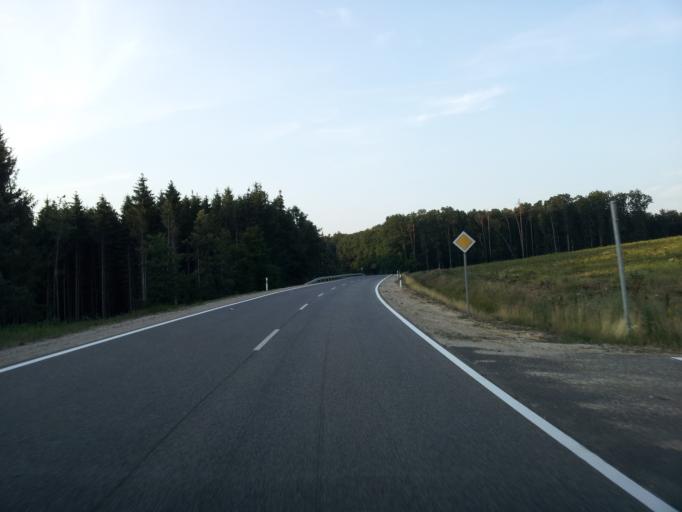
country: HU
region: Zala
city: Zalalovo
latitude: 46.7840
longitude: 16.5663
